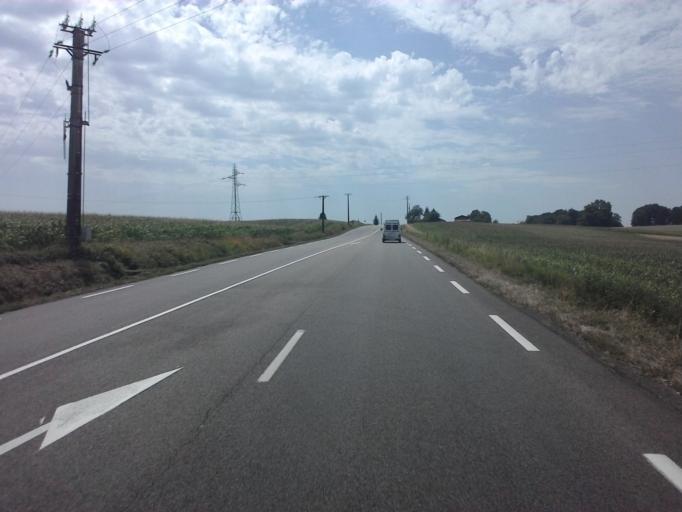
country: FR
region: Rhone-Alpes
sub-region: Departement de l'Ain
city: Saint-Etienne-du-Bois
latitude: 46.3102
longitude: 5.3040
